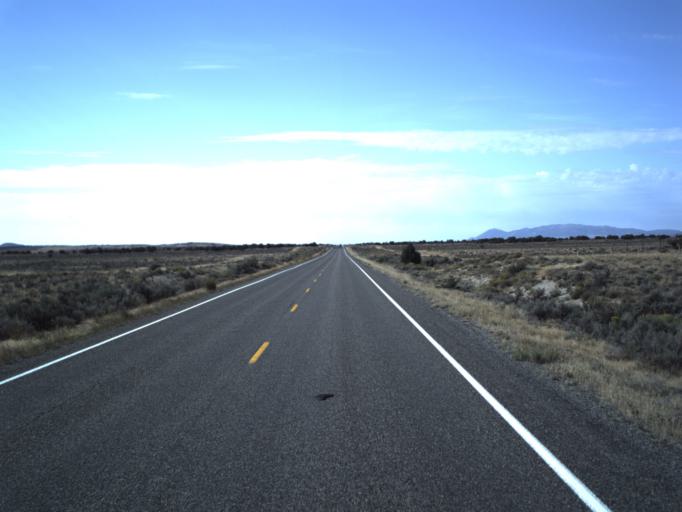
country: US
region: Idaho
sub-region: Cassia County
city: Burley
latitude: 41.7263
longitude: -113.5245
